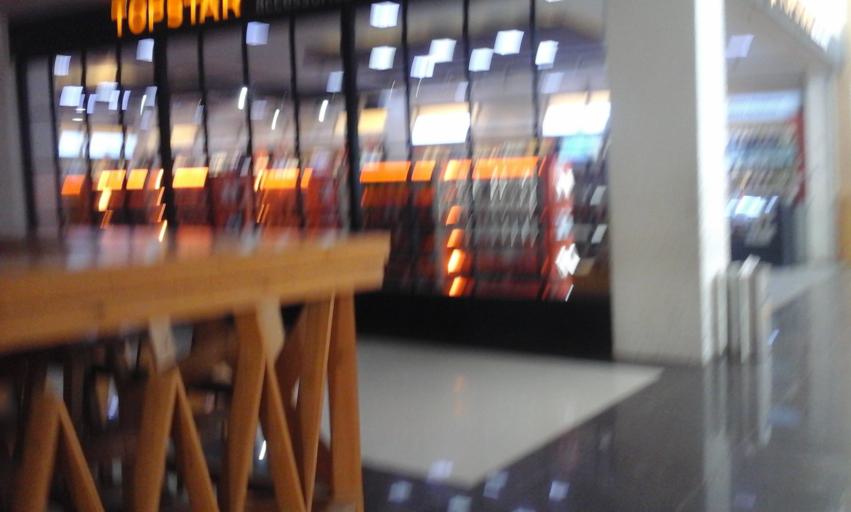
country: ID
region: East Java
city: Krajan
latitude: -8.1830
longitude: 113.6631
